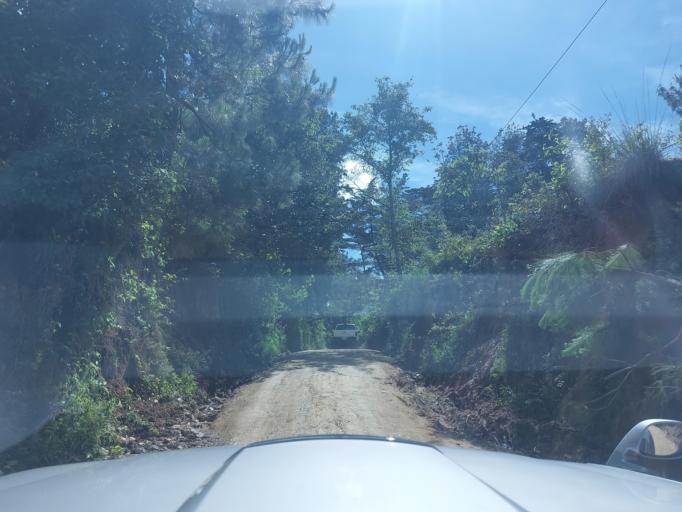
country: GT
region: Chimaltenango
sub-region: Municipio de San Juan Comalapa
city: Comalapa
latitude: 14.7550
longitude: -90.8893
